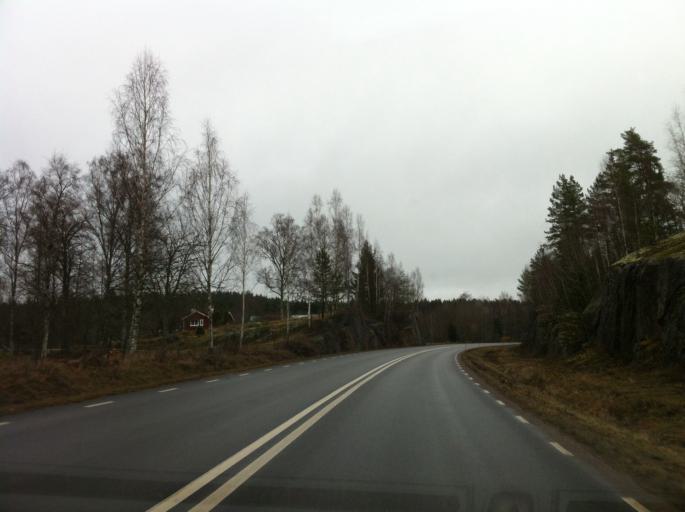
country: SE
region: Kalmar
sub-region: Vimmerby Kommun
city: Sodra Vi
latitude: 57.8907
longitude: 15.7762
